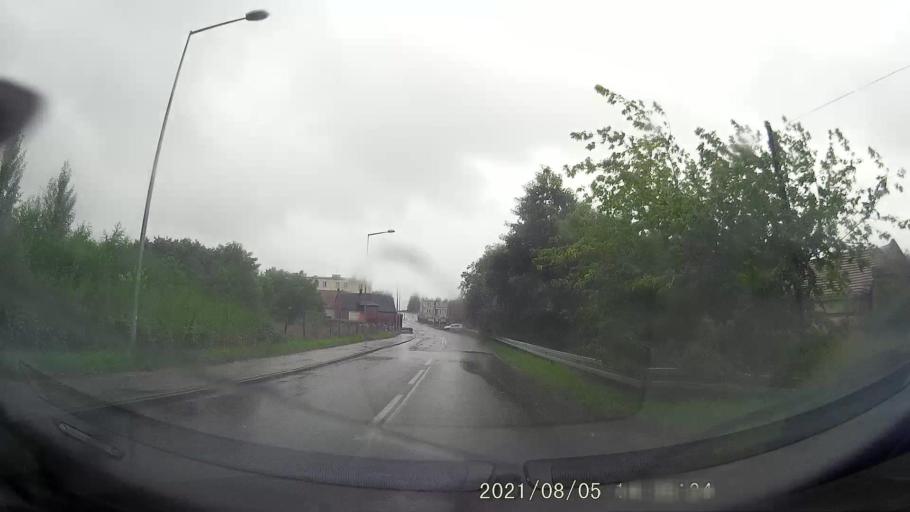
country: PL
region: Opole Voivodeship
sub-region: Powiat nyski
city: Lambinowice
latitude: 50.4672
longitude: 17.5032
